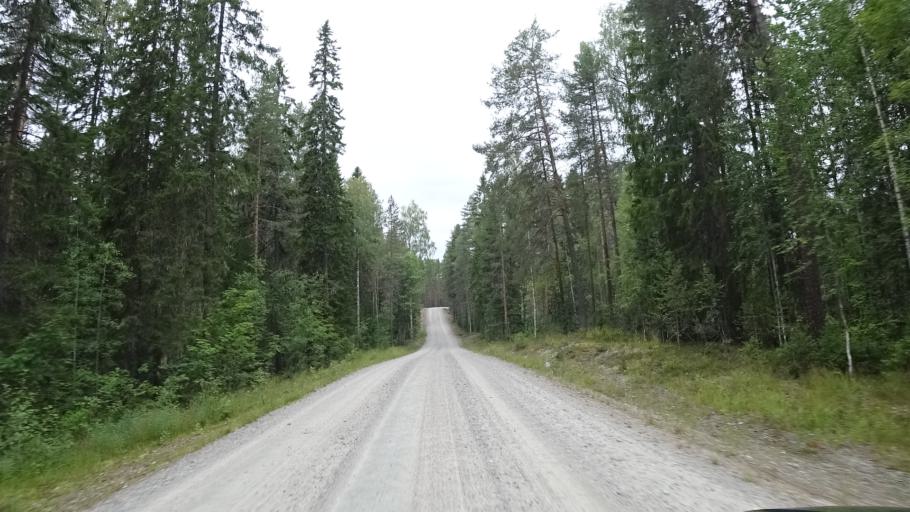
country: FI
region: North Karelia
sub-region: Pielisen Karjala
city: Lieksa
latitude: 63.2075
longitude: 30.4242
